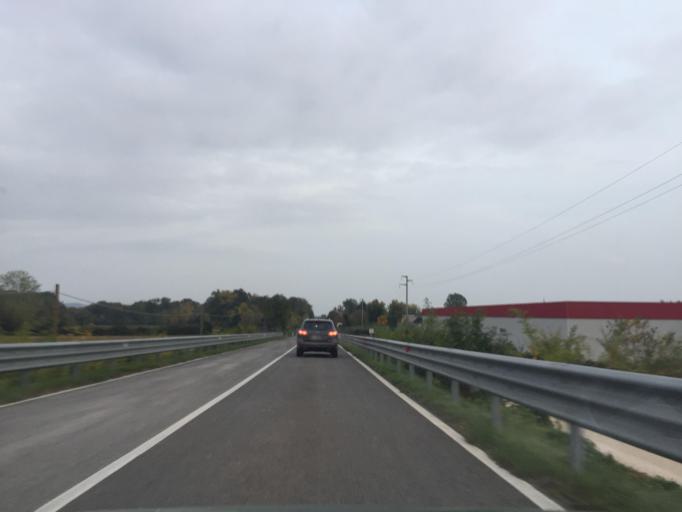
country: IT
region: Friuli Venezia Giulia
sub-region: Provincia di Pordenone
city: Fanna
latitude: 46.1740
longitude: 12.7298
